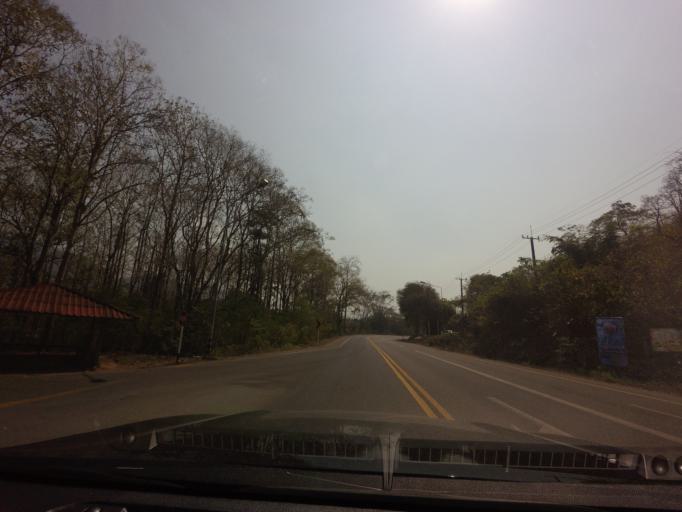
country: TH
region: Kanchanaburi
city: Thong Pha Phum
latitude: 14.7780
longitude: 98.6038
